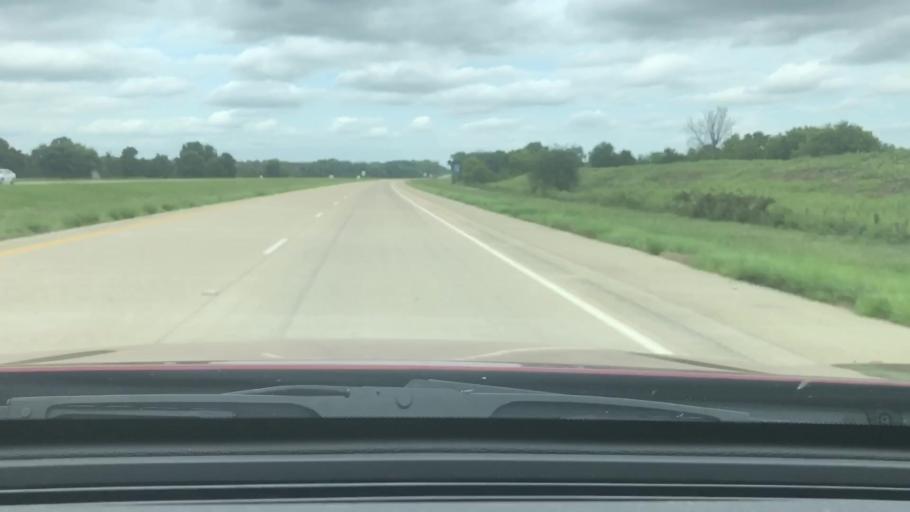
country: US
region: Louisiana
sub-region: Caddo Parish
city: Oil City
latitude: 32.7760
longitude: -93.8893
